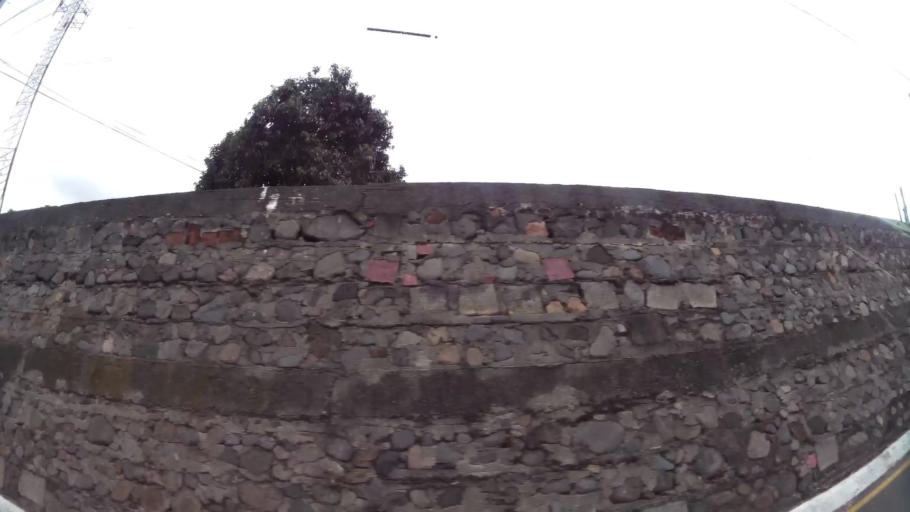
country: GT
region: Guatemala
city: Guatemala City
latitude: 14.6361
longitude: -90.5508
